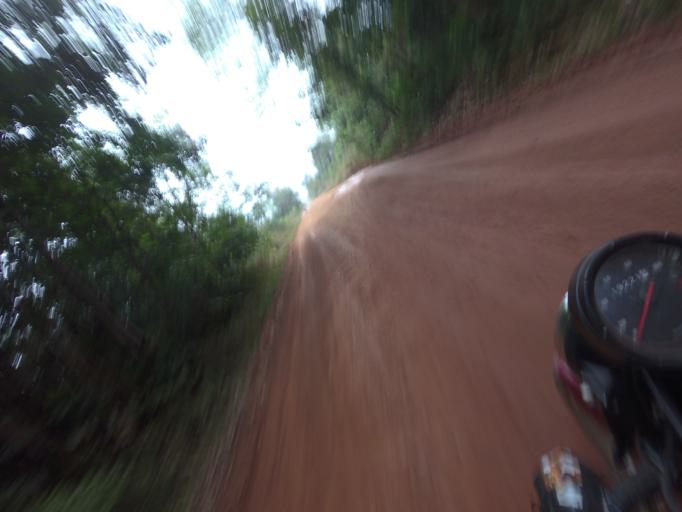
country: LR
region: Nimba
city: Sanniquellie
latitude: 7.4066
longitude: -8.6582
